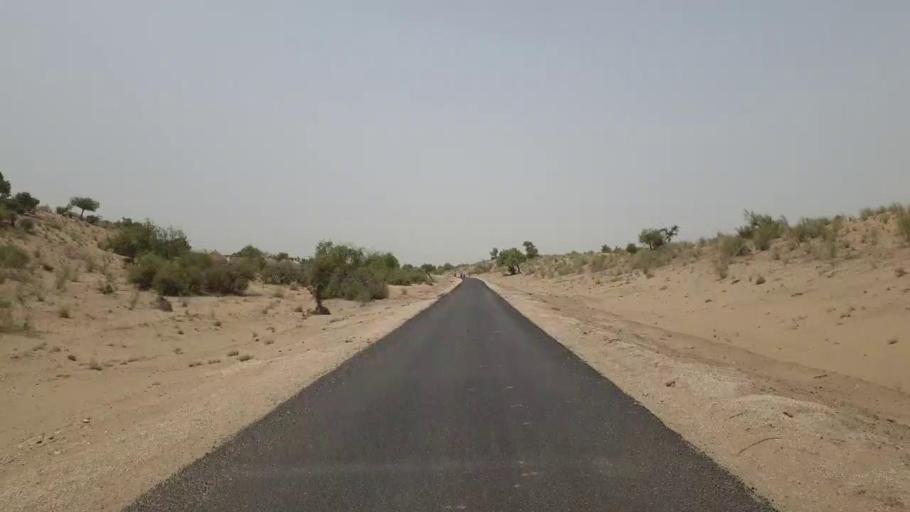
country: PK
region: Sindh
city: Islamkot
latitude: 24.8022
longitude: 70.5538
